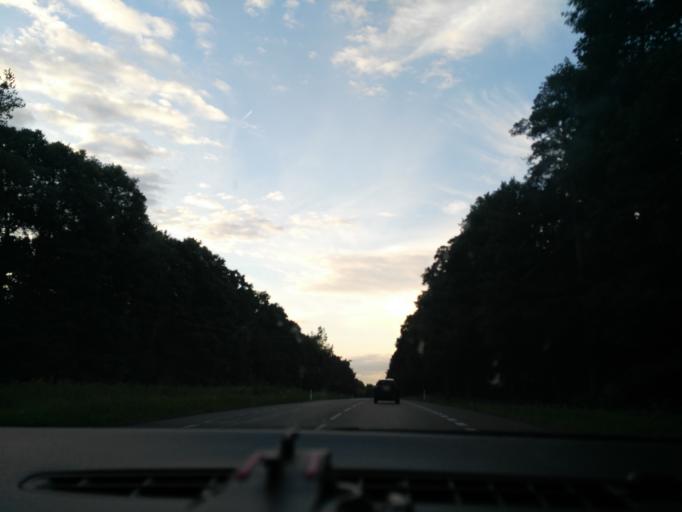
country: PL
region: Lublin Voivodeship
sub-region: Powiat lubelski
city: Niemce
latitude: 51.3776
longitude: 22.6346
